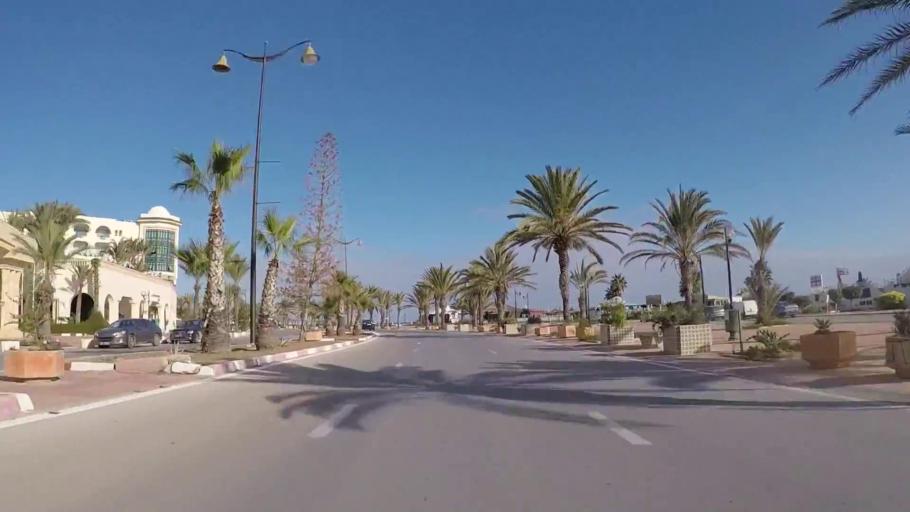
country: TN
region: Nabul
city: Al Hammamat
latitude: 36.3633
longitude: 10.5352
